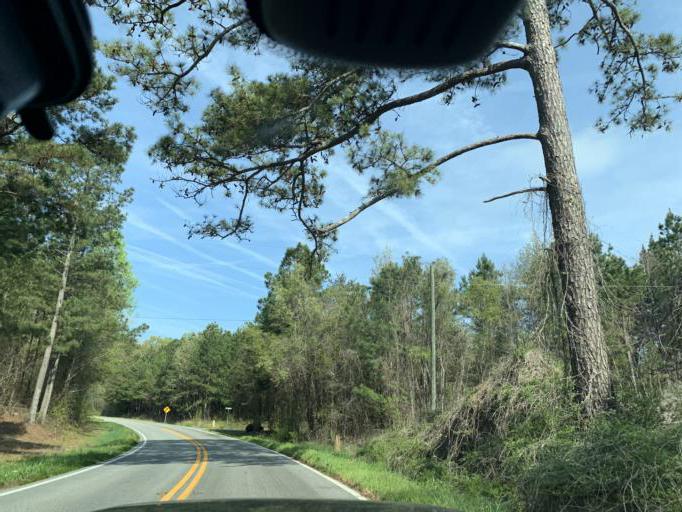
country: US
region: Georgia
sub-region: Forsyth County
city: Cumming
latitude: 34.2076
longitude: -84.0705
